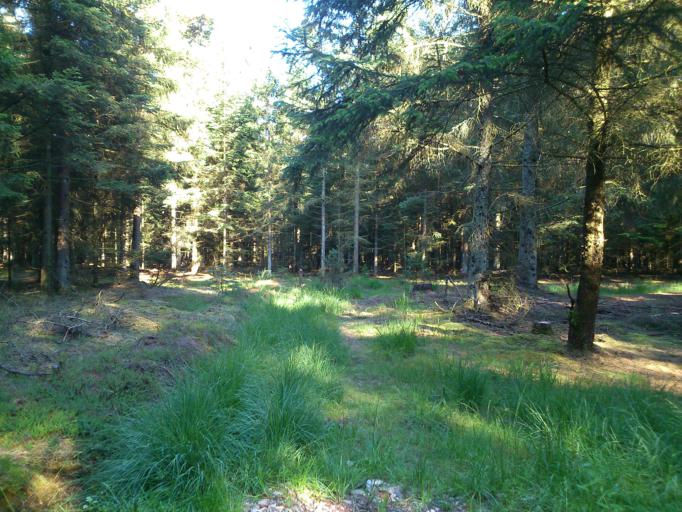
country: DK
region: Central Jutland
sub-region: Ringkobing-Skjern Kommune
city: Tarm
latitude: 55.8998
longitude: 8.5509
